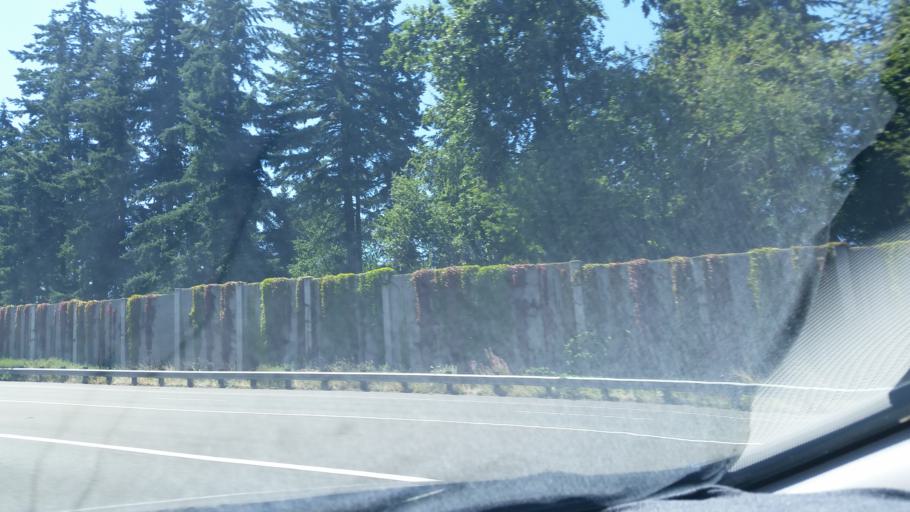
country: US
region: Oregon
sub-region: Washington County
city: Tualatin
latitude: 45.3624
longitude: -122.7609
